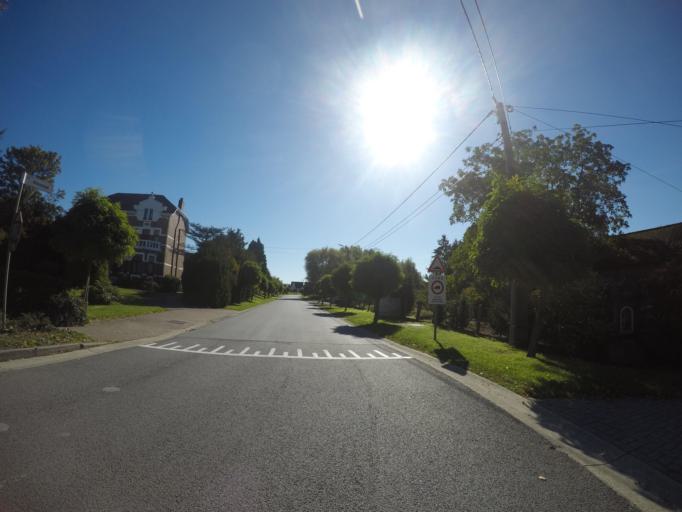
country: BE
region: Flanders
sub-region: Provincie Limburg
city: Alken
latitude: 50.8778
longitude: 5.3152
